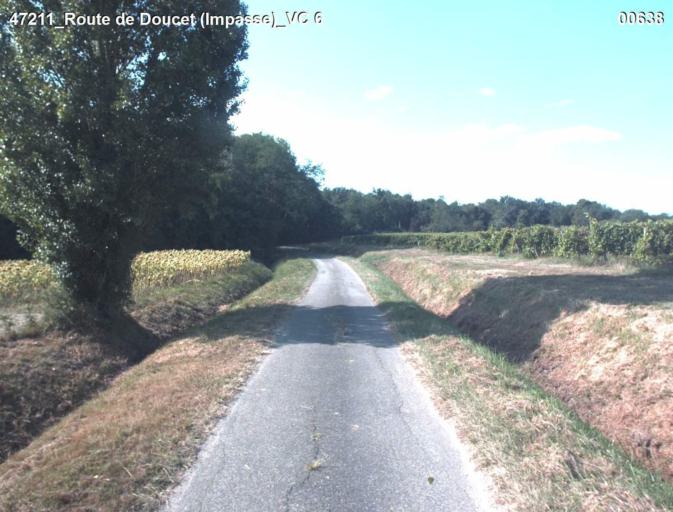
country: FR
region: Midi-Pyrenees
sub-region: Departement du Gers
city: Montreal
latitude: 44.0171
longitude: 0.2014
